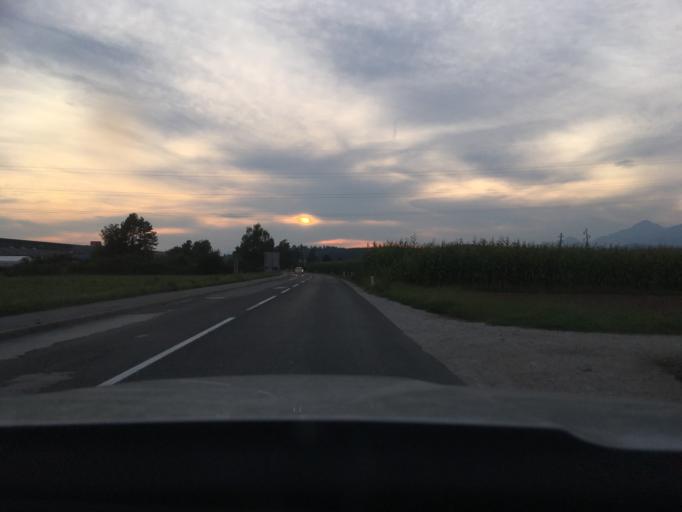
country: SI
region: Kamnik
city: Smarca
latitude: 46.1986
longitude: 14.5911
